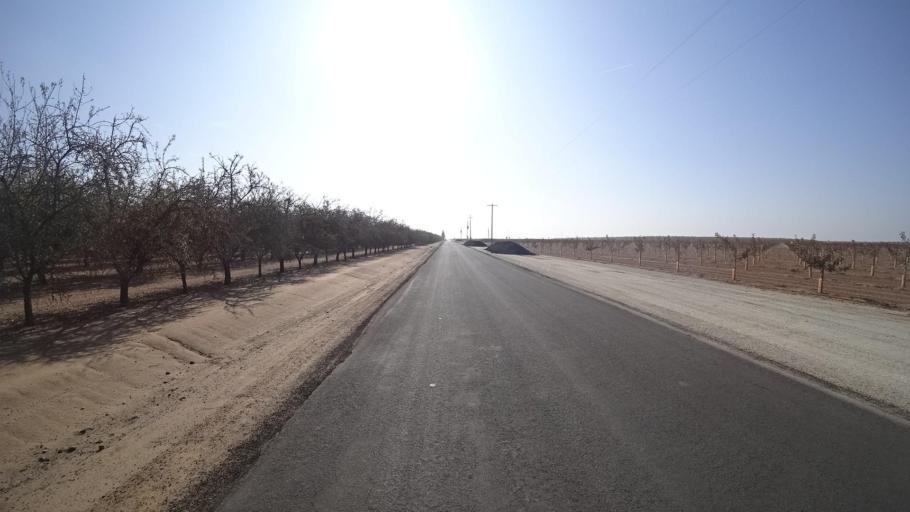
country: US
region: California
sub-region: Kern County
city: McFarland
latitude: 35.6365
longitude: -119.1866
